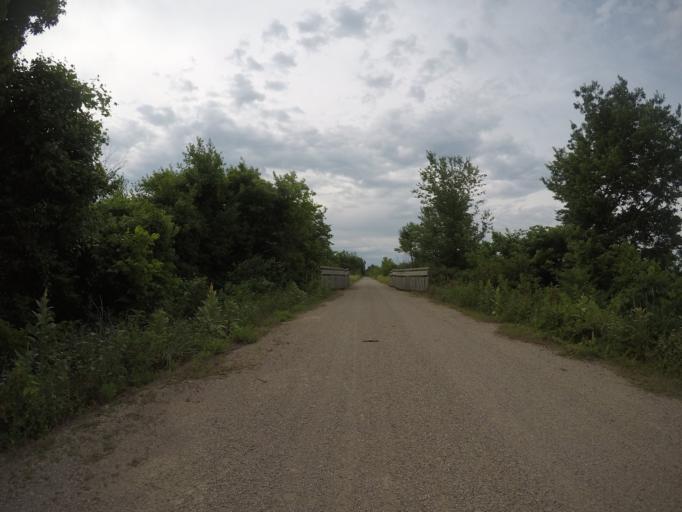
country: US
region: Kansas
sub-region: Franklin County
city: Ottawa
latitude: 38.4572
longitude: -95.2691
